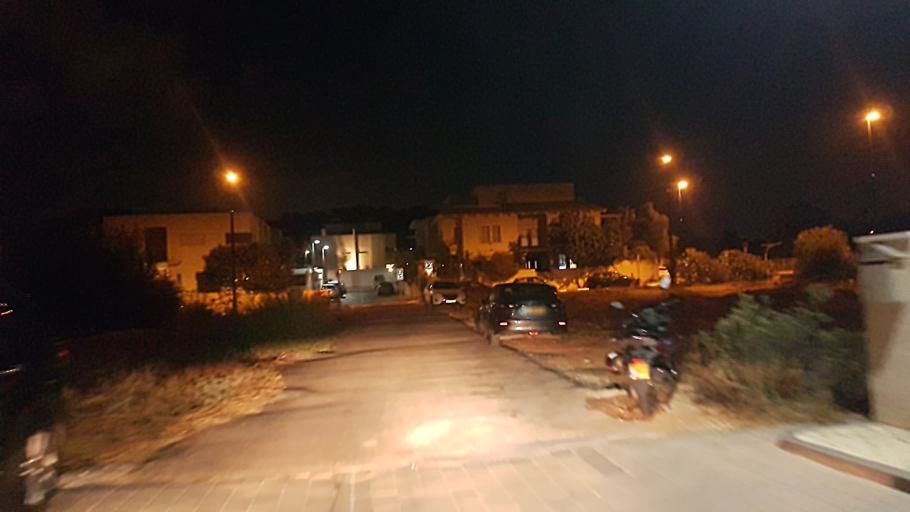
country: IL
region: Central District
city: Hod HaSharon
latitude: 32.1653
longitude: 34.8911
